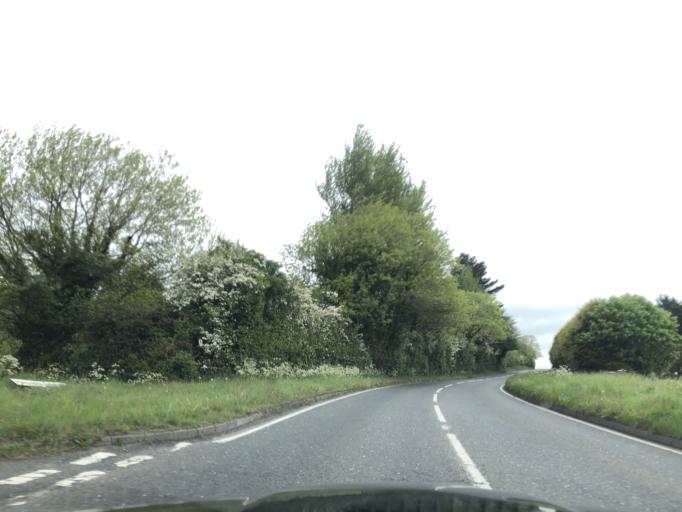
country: GB
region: Northern Ireland
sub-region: Lisburn District
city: Lisburn
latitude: 54.5394
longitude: -6.0753
